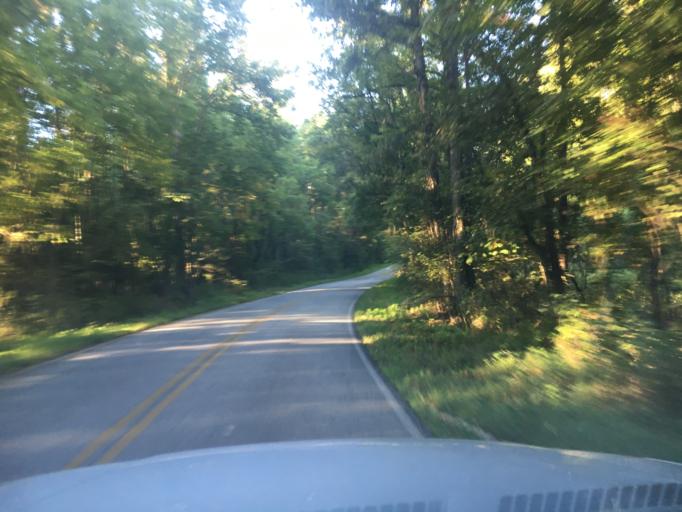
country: US
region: South Carolina
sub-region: Spartanburg County
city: Woodruff
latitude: 34.6736
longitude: -81.9622
